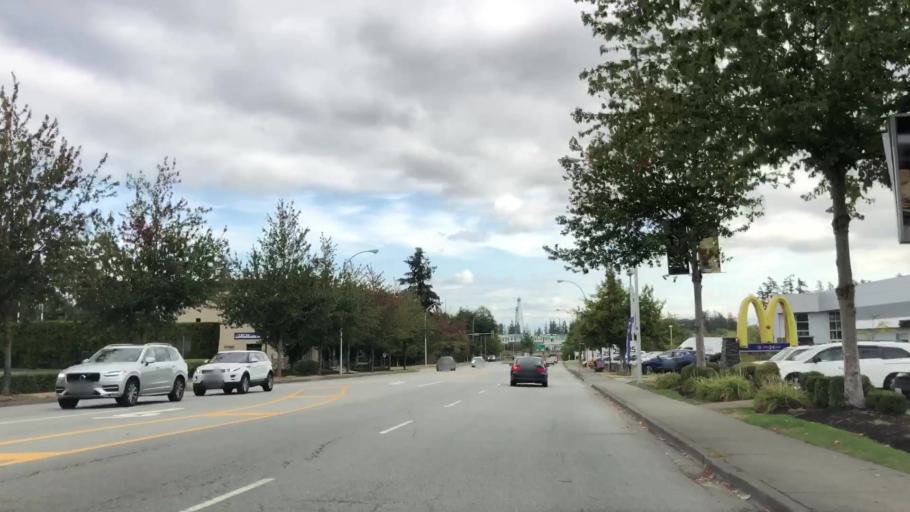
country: CA
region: British Columbia
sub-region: Greater Vancouver Regional District
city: White Rock
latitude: 49.0590
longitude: -122.8095
